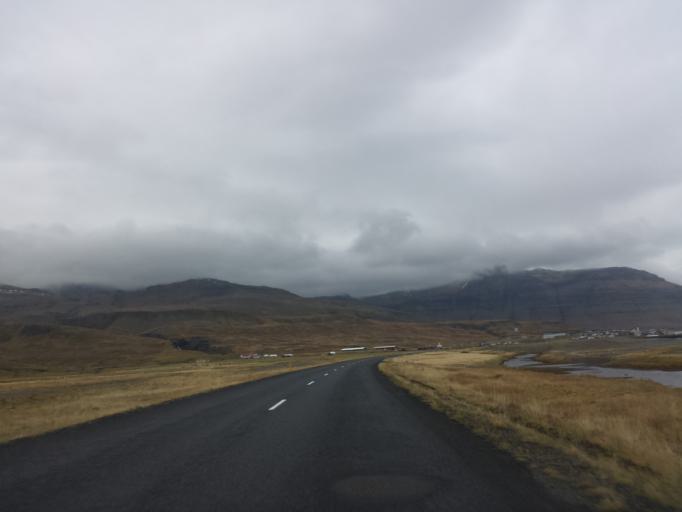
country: IS
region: West
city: Olafsvik
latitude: 64.9233
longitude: -23.2185
